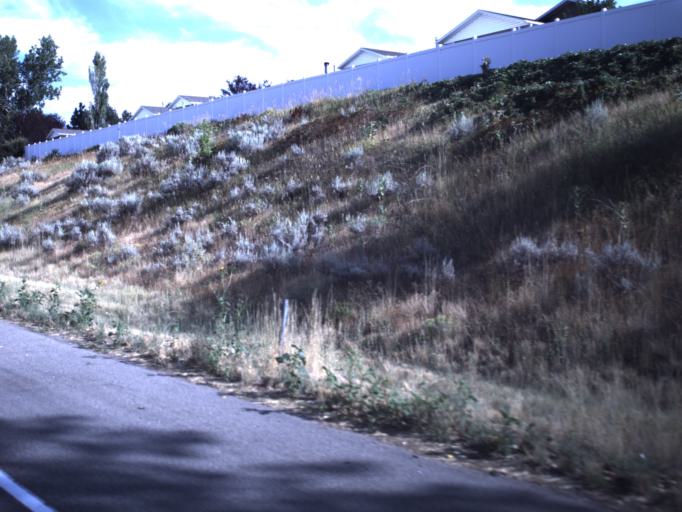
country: US
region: Utah
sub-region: Weber County
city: Washington Terrace
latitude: 41.1623
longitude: -111.9501
